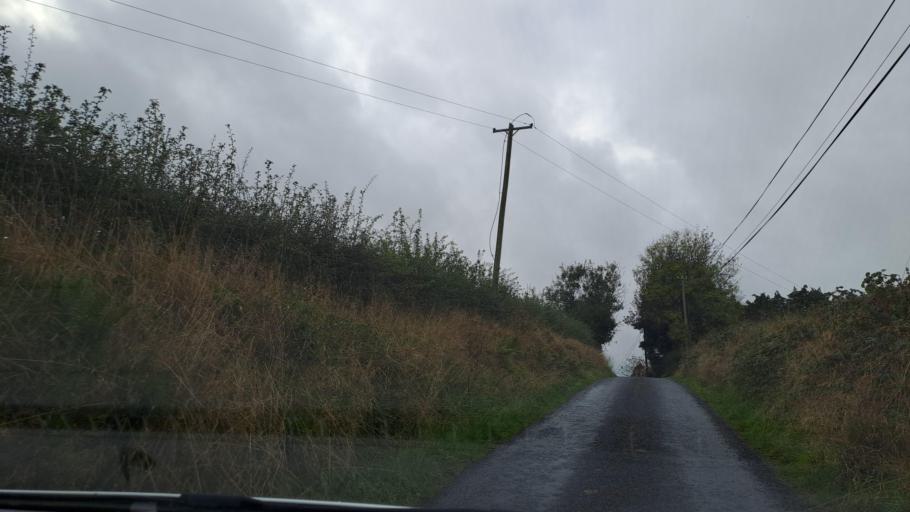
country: IE
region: Ulster
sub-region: An Cabhan
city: Kingscourt
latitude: 53.9368
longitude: -6.8555
